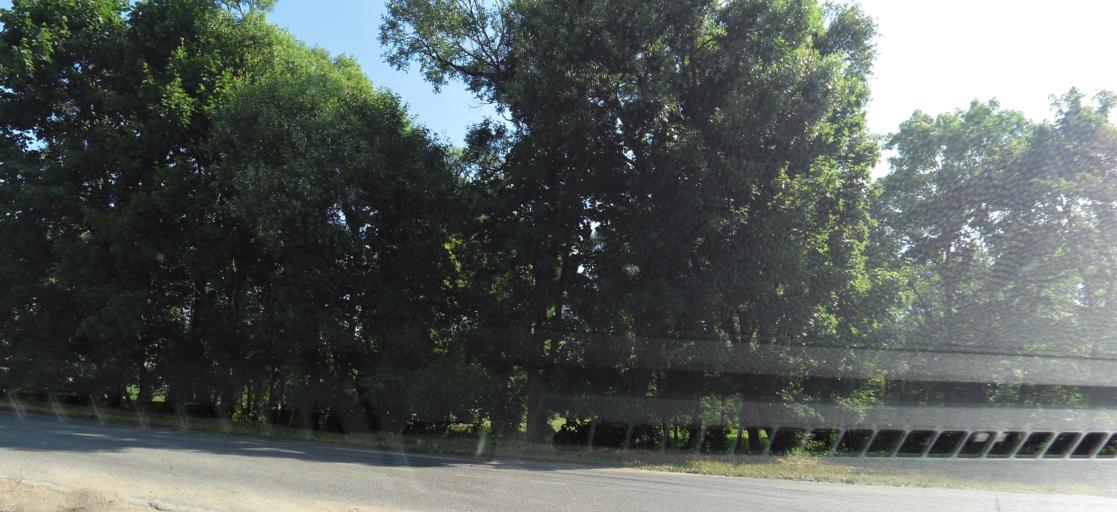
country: LT
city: Grigiskes
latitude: 54.8663
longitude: 25.0680
